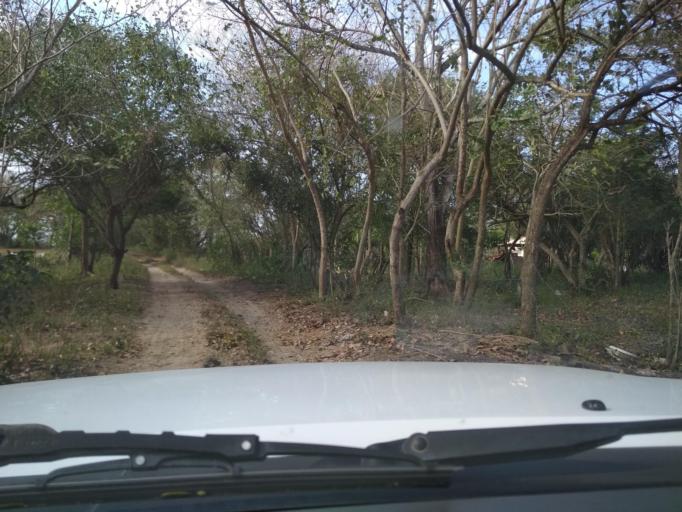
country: MX
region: Veracruz
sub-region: Veracruz
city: Delfino Victoria (Santa Fe)
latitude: 19.1538
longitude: -96.3011
